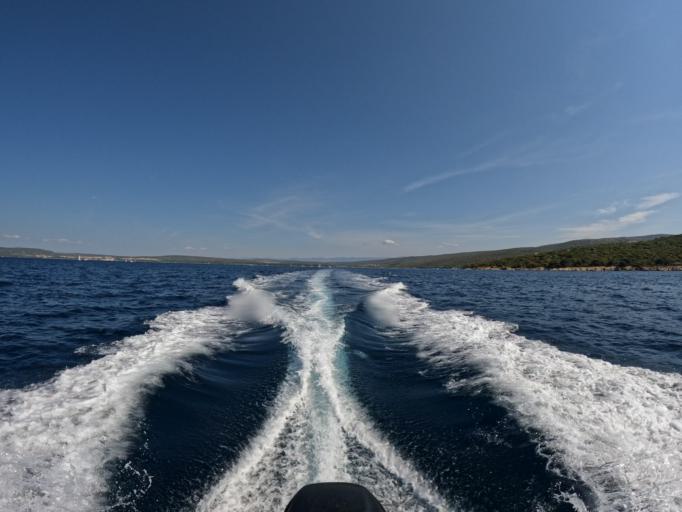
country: HR
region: Primorsko-Goranska
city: Punat
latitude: 44.9798
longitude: 14.6107
